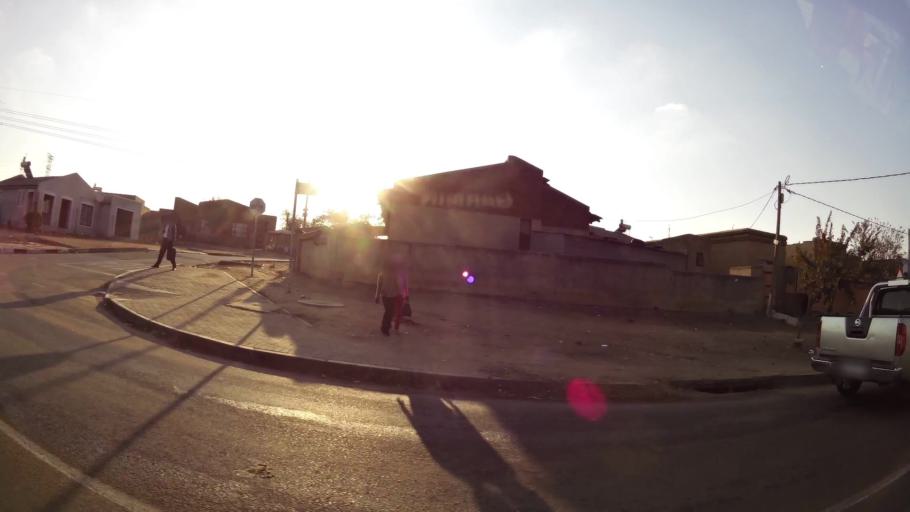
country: ZA
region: Gauteng
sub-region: Ekurhuleni Metropolitan Municipality
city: Tembisa
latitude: -26.0167
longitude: 28.1823
